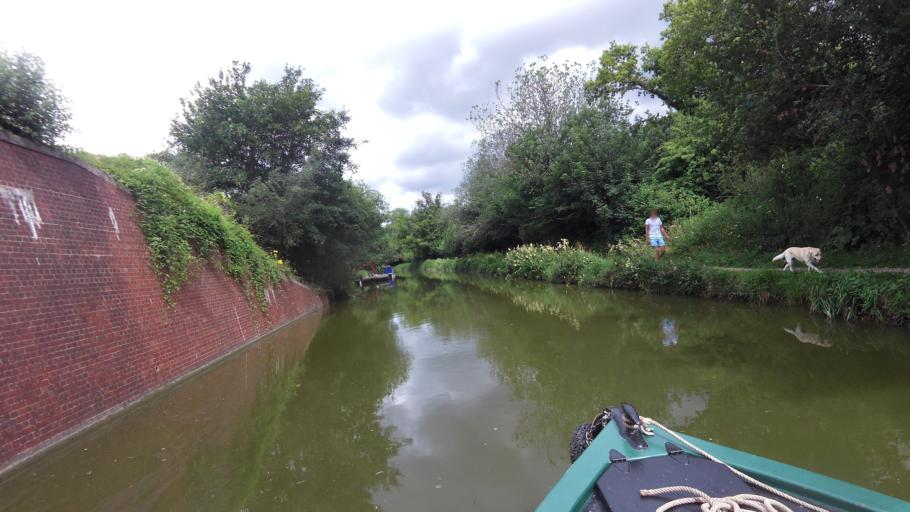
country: GB
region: England
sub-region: West Berkshire
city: Kintbury
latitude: 51.4089
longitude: -1.4740
